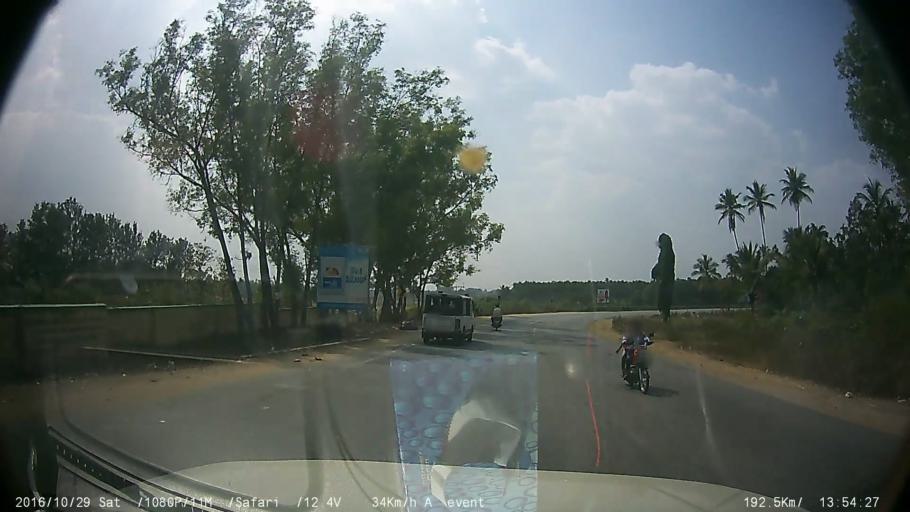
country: IN
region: Karnataka
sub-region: Mysore
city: Piriyapatna
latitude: 12.3373
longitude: 76.1780
